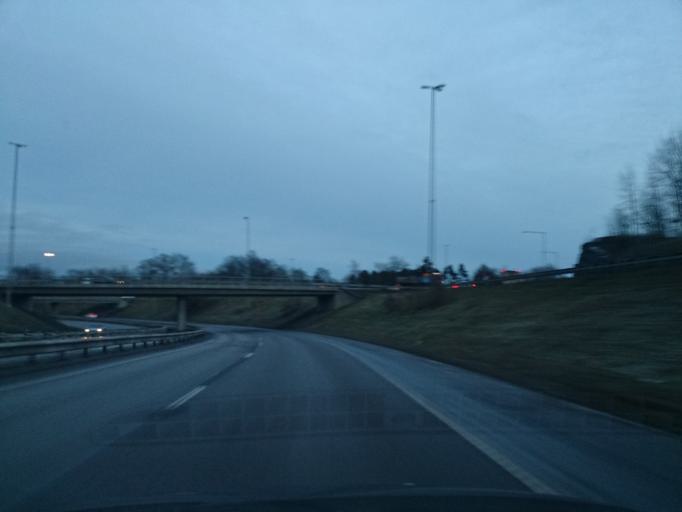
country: SE
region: OEstergoetland
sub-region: Norrkopings Kommun
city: Norrkoping
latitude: 58.5836
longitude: 16.1470
